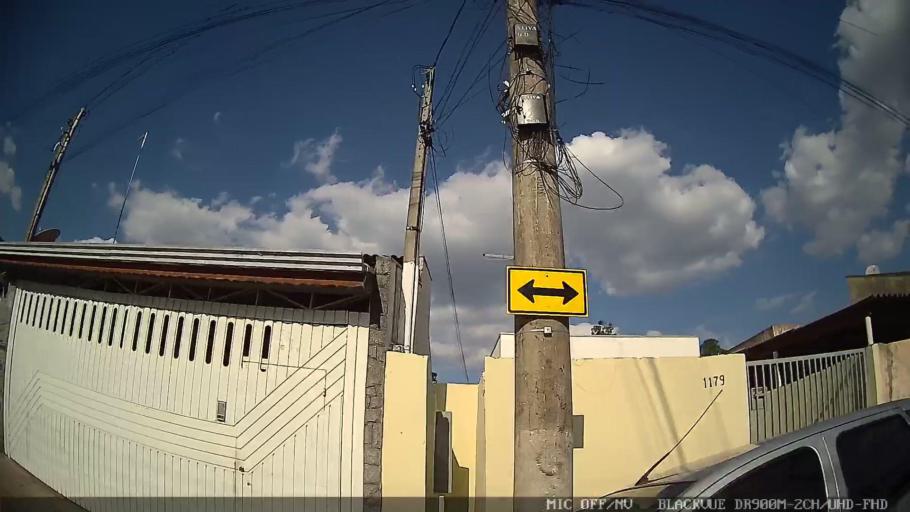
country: BR
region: Sao Paulo
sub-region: Cabreuva
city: Cabreuva
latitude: -23.2547
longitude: -47.0580
